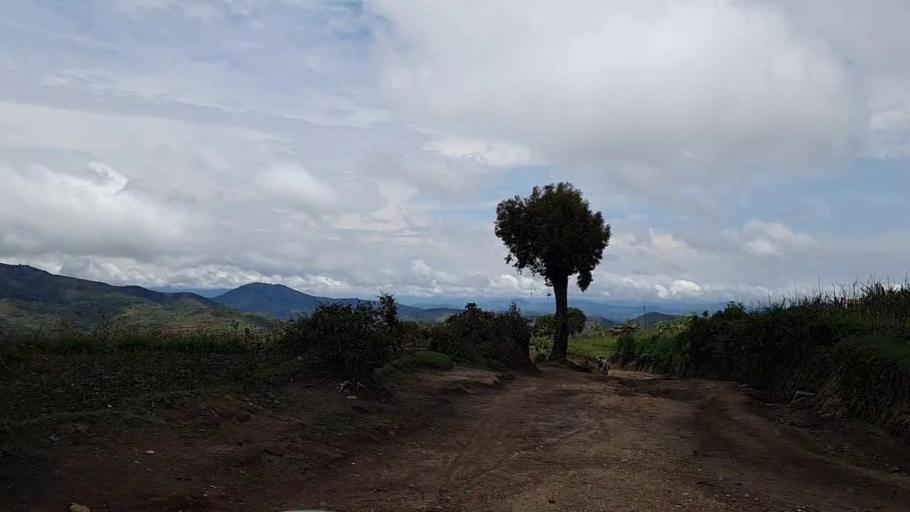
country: RW
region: Southern Province
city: Gikongoro
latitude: -2.3444
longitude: 29.5077
